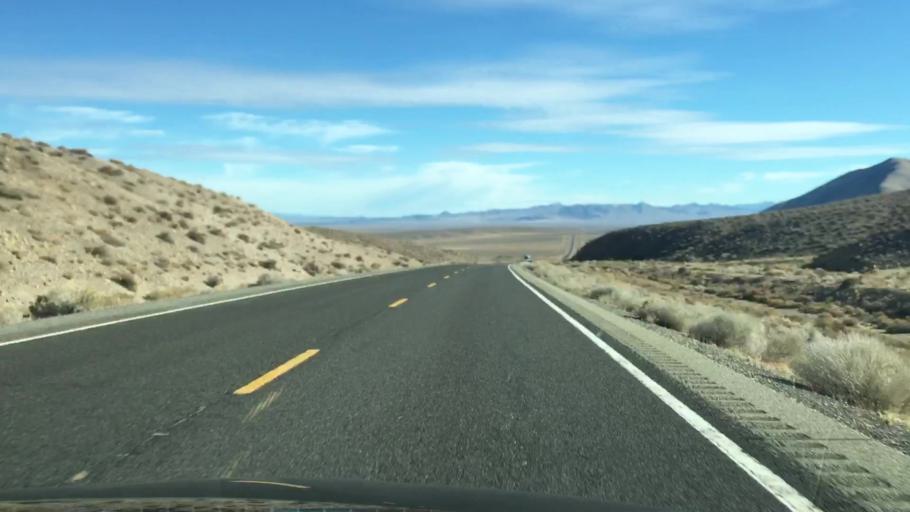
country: US
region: Nevada
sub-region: Lyon County
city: Yerington
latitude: 39.0368
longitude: -118.9298
